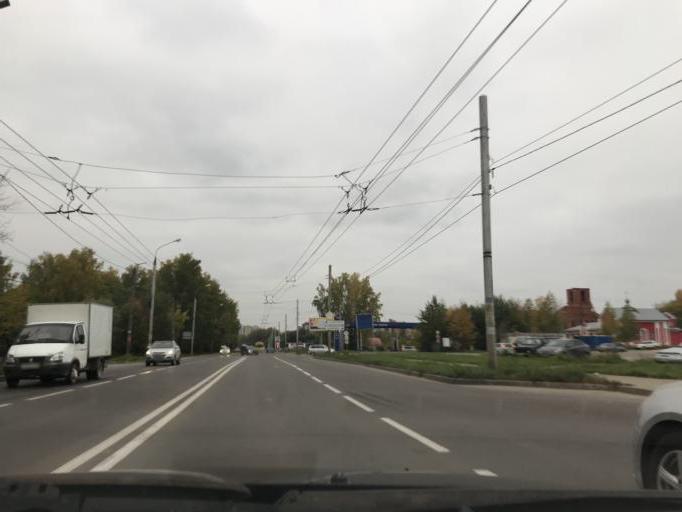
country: RU
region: Kaluga
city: Kaluga
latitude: 54.5979
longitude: 36.2606
